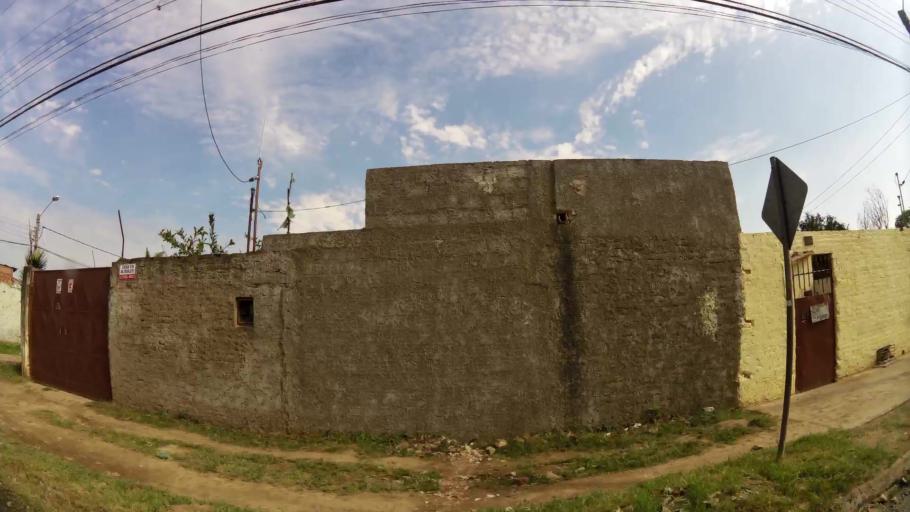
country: BO
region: Santa Cruz
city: Santa Cruz de la Sierra
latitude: -17.7218
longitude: -63.1370
